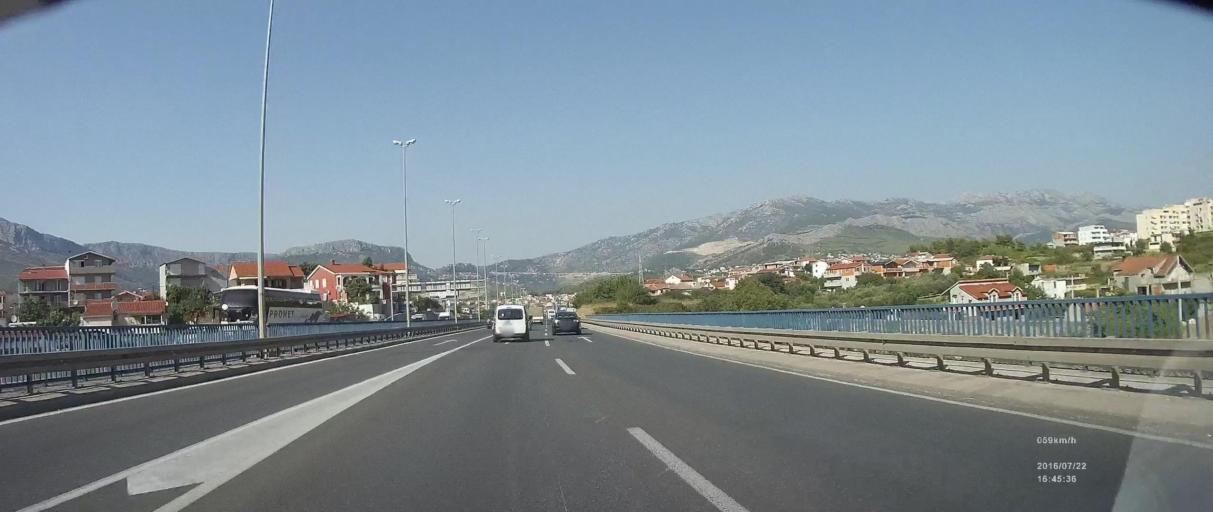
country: HR
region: Splitsko-Dalmatinska
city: Vranjic
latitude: 43.5204
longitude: 16.4828
